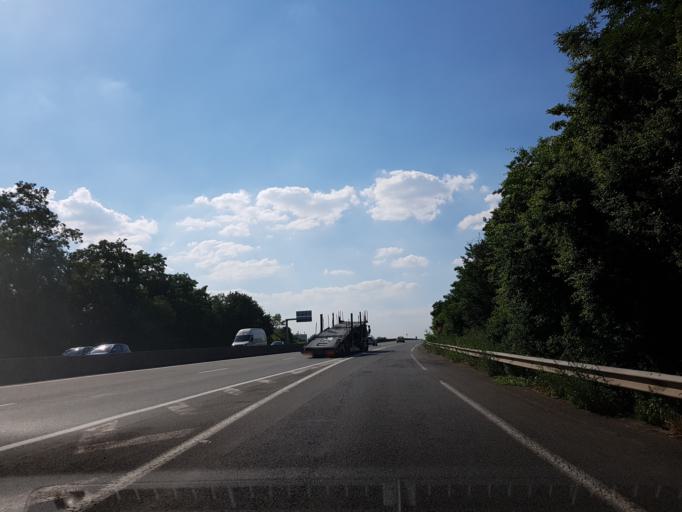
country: FR
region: Nord-Pas-de-Calais
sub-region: Departement du Nord
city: Escaudain
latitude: 50.3263
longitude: 3.3392
